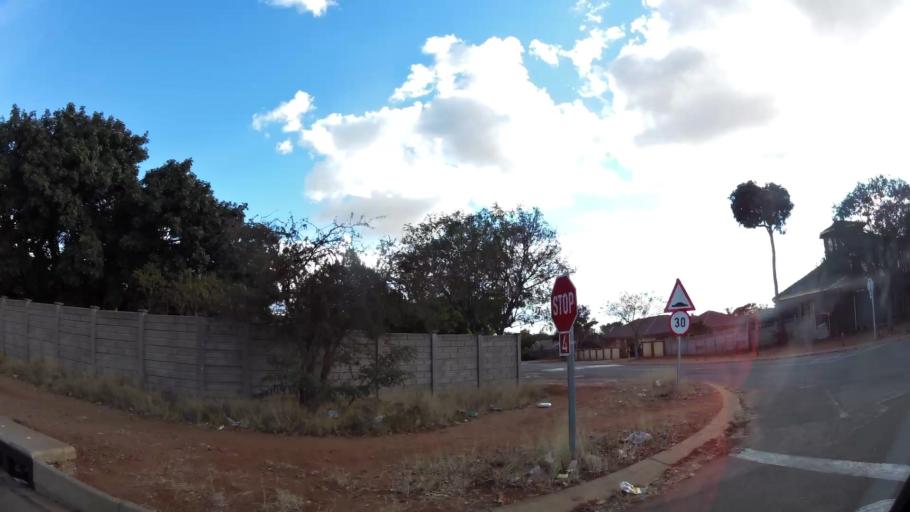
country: ZA
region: Limpopo
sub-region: Capricorn District Municipality
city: Polokwane
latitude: -23.9110
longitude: 29.4957
